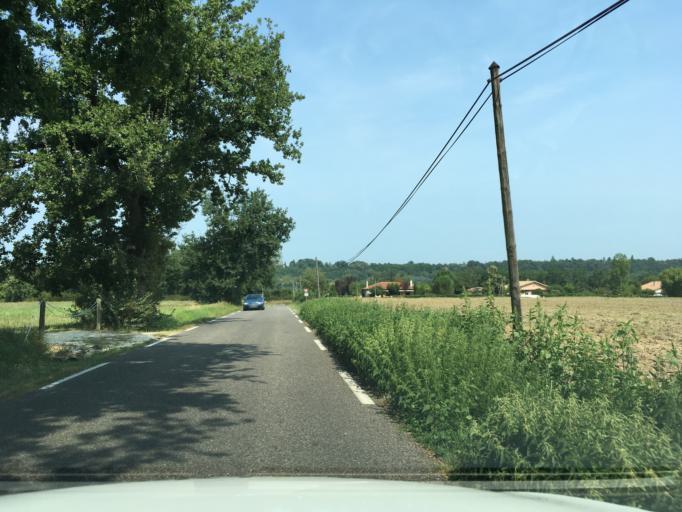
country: FR
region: Midi-Pyrenees
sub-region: Departement du Tarn-et-Garonne
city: Montauban
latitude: 43.9899
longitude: 1.3756
